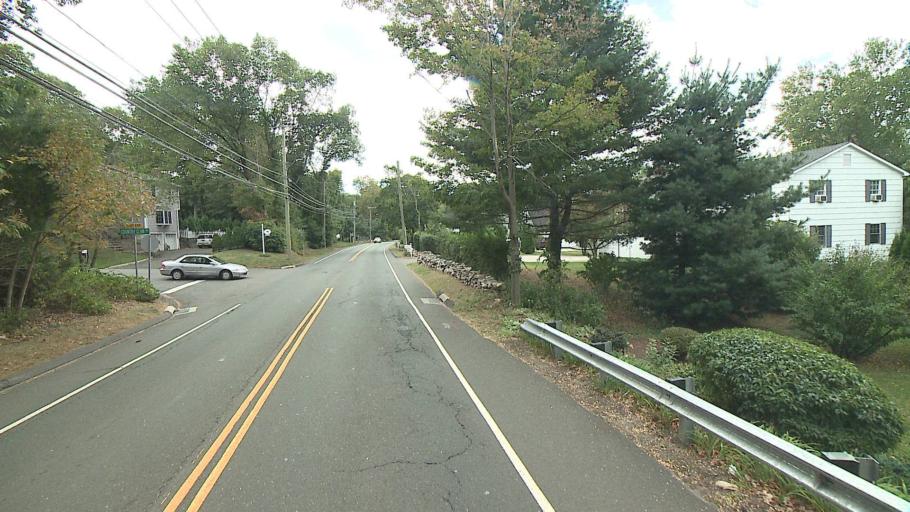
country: US
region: Connecticut
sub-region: Fairfield County
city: New Canaan
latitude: 41.1103
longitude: -73.5011
